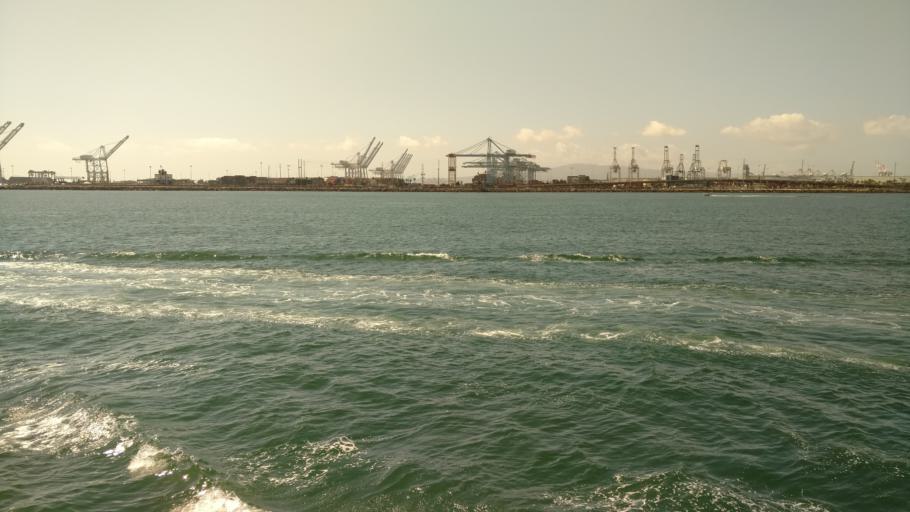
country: US
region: California
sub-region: Los Angeles County
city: Long Beach
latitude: 33.7451
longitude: -118.1797
